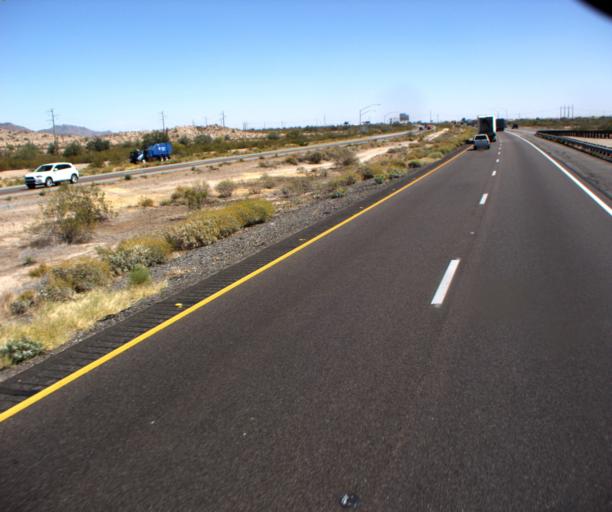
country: US
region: Arizona
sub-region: Maricopa County
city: Buckeye
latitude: 33.4269
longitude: -112.6201
